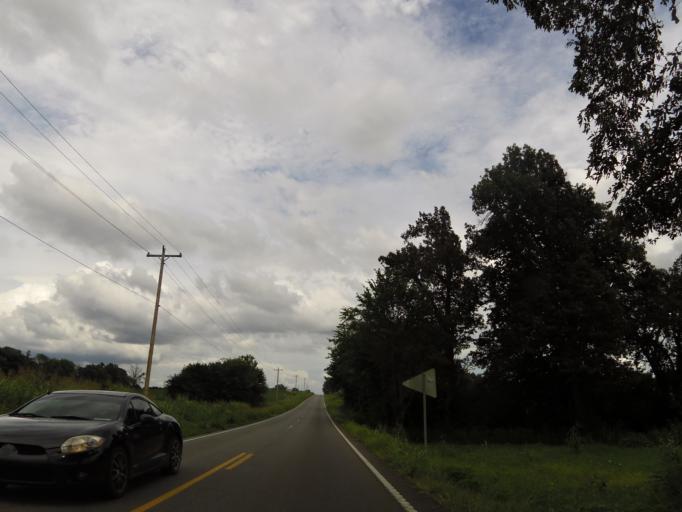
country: US
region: Kentucky
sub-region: Ballard County
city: La Center
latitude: 36.9905
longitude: -88.9293
